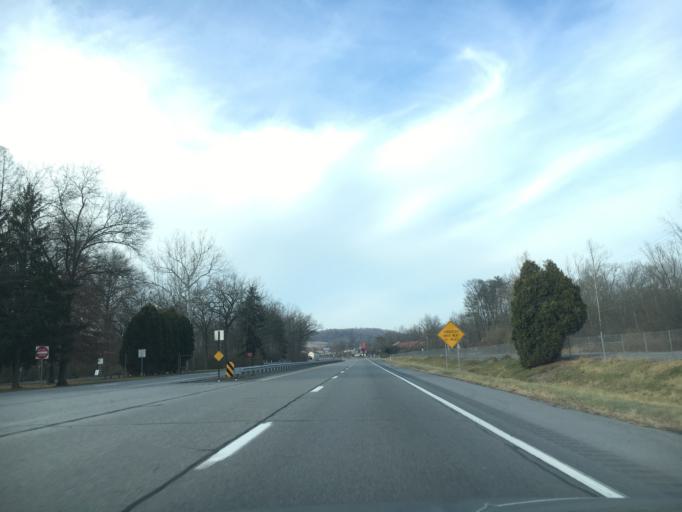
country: US
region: Pennsylvania
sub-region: Montour County
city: Danville
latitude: 40.9907
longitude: -76.6355
